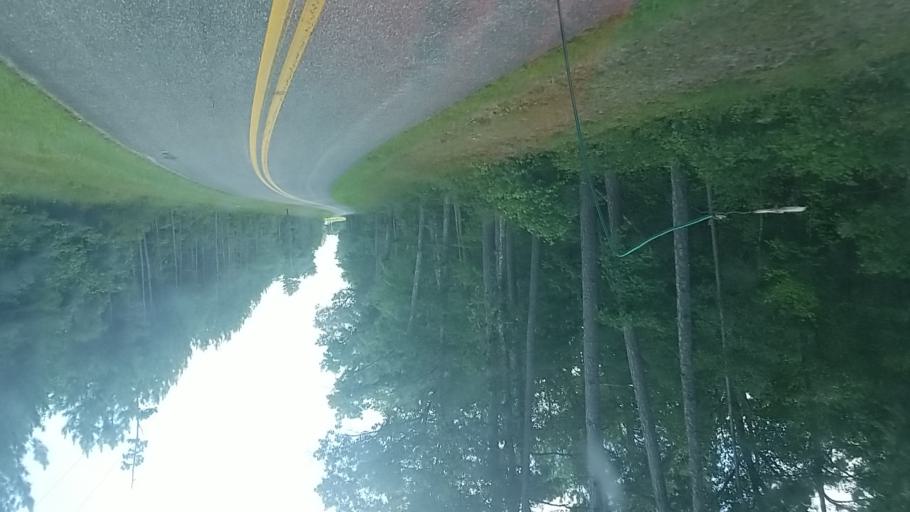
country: US
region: Maryland
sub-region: Worcester County
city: Snow Hill
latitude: 38.2574
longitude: -75.4459
